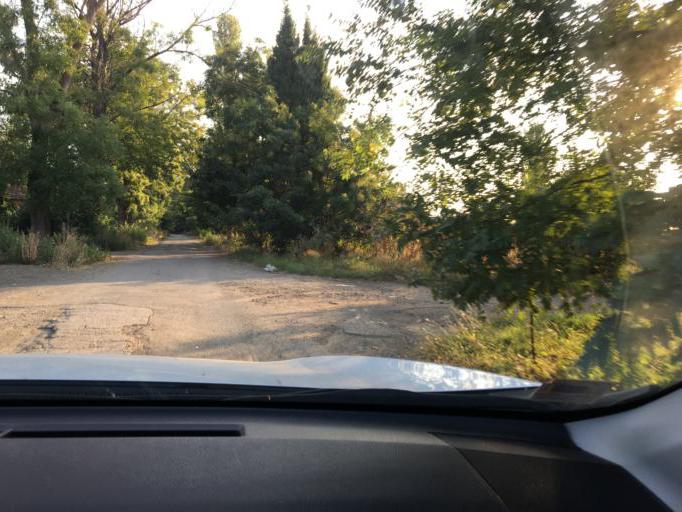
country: BG
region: Burgas
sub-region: Obshtina Burgas
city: Burgas
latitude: 42.6087
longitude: 27.4867
